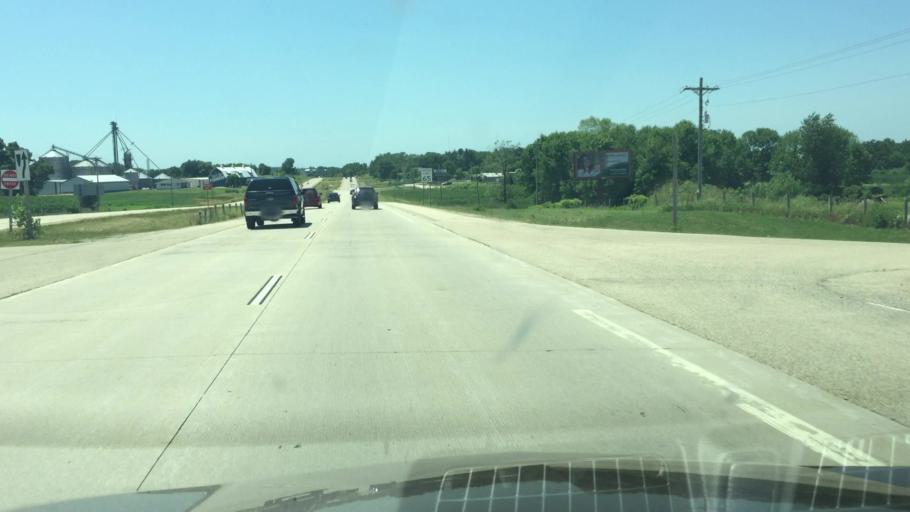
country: US
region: Wisconsin
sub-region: Dodge County
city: Beaver Dam
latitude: 43.4315
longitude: -88.8773
